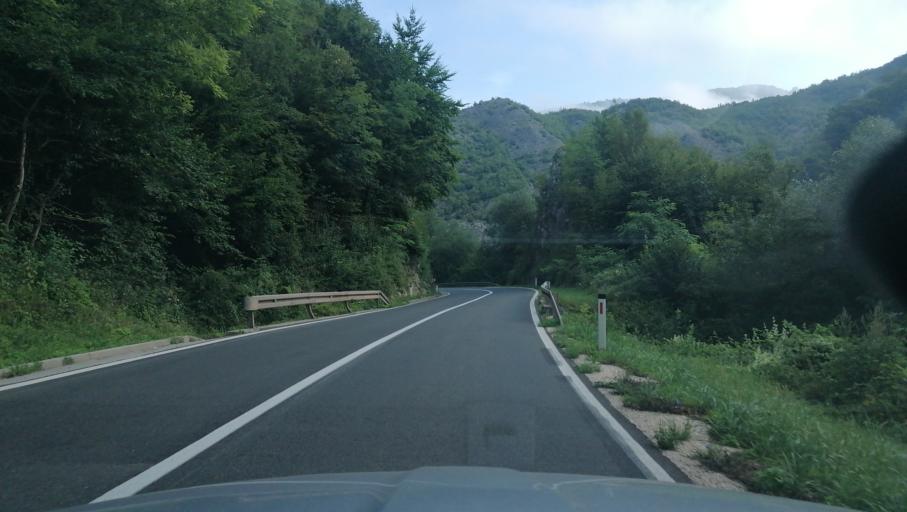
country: BA
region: Federation of Bosnia and Herzegovina
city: Jajce
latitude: 44.4001
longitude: 17.2710
